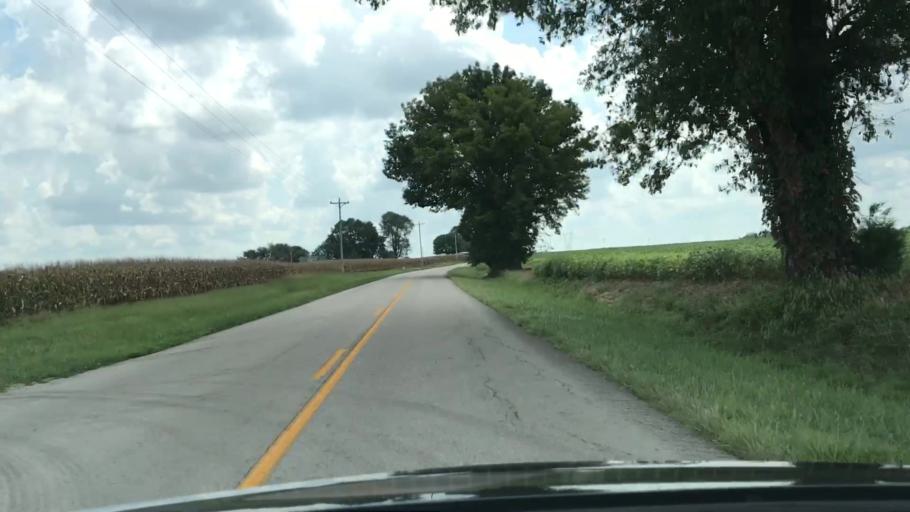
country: US
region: Kentucky
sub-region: Todd County
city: Elkton
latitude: 36.7813
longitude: -87.1232
